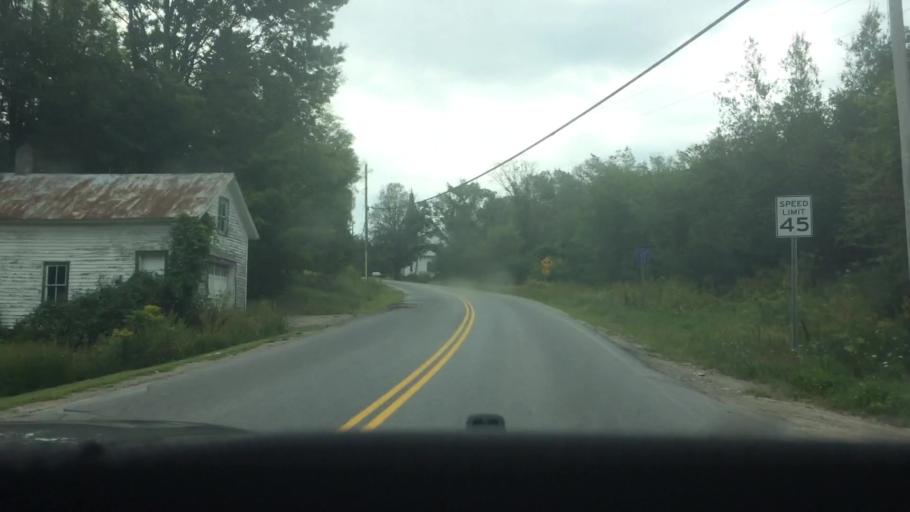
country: US
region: New York
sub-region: St. Lawrence County
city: Canton
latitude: 44.4987
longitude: -75.3427
